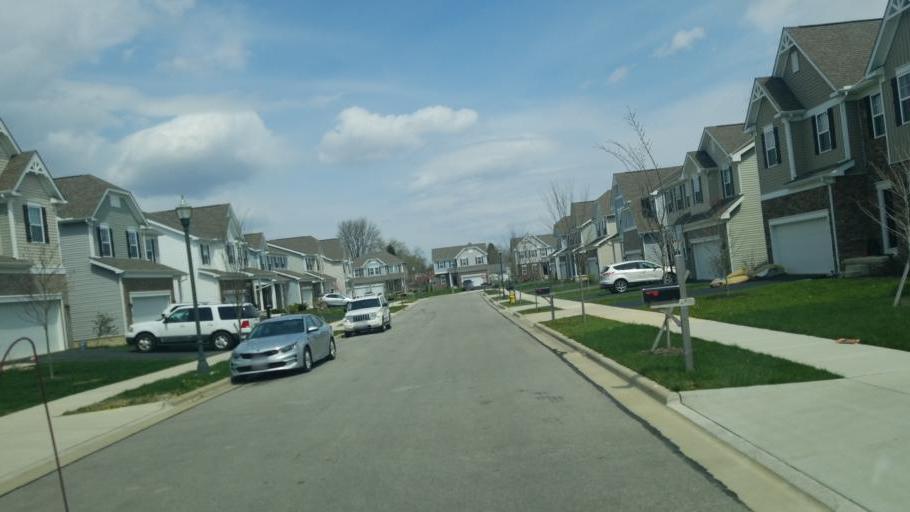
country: US
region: Ohio
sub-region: Delaware County
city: Delaware
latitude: 40.2929
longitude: -83.0922
